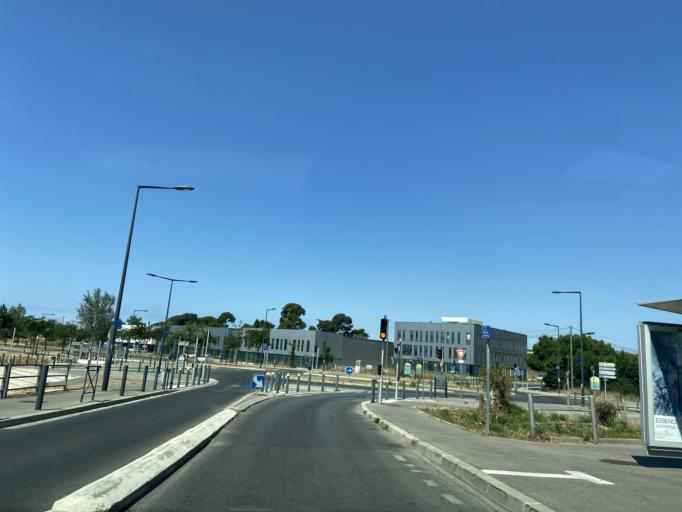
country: FR
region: Provence-Alpes-Cote d'Azur
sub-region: Departement des Bouches-du-Rhone
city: Plan-de-Cuques
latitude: 43.3428
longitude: 5.4464
